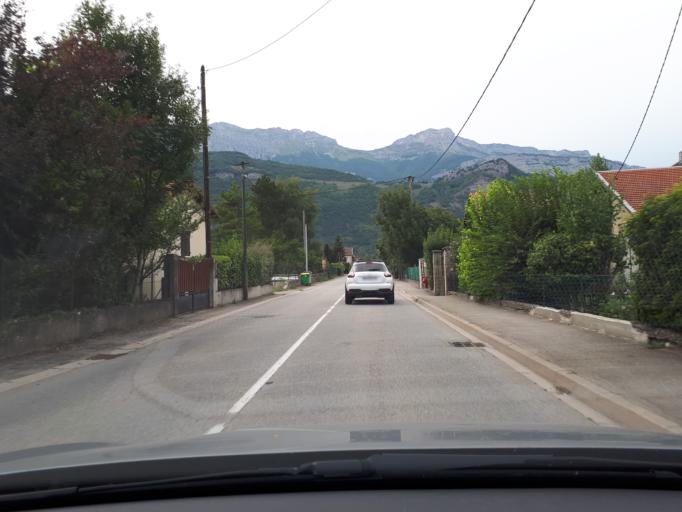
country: FR
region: Rhone-Alpes
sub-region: Departement de l'Isere
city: Vif
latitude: 45.0506
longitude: 5.6818
